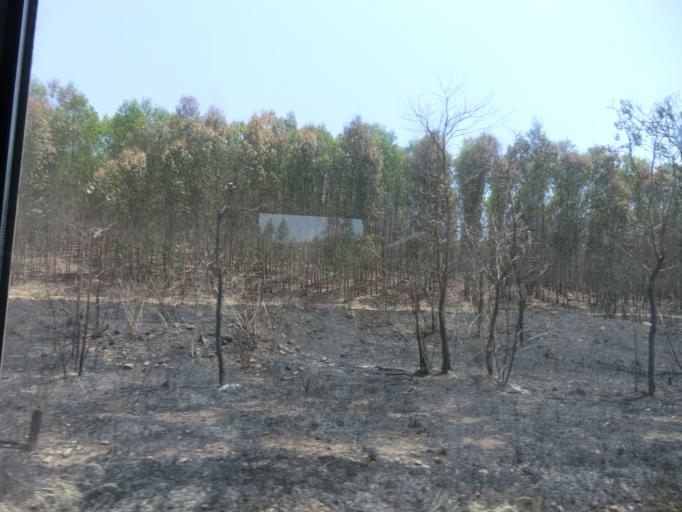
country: VN
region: Binh Thuan
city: Thuan Nam
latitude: 10.9217
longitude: 107.8864
